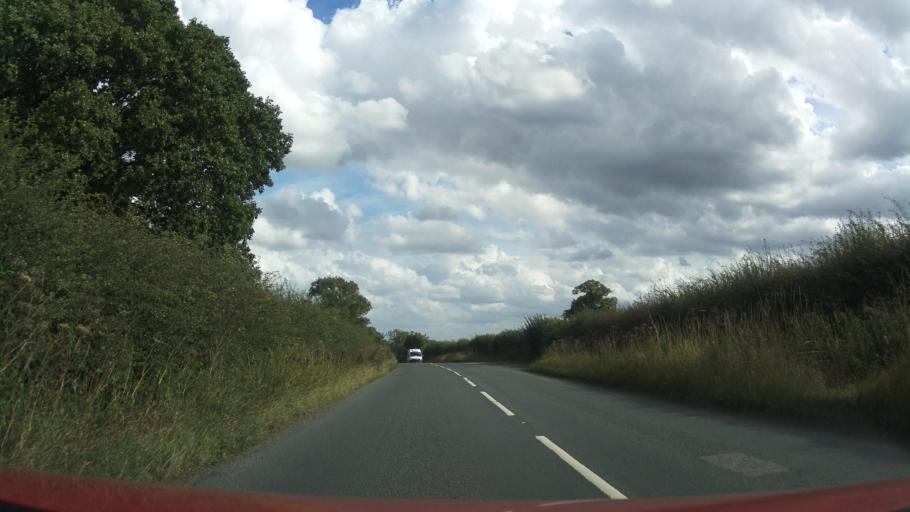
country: GB
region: England
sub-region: North Yorkshire
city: Bedale
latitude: 54.2079
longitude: -1.6054
